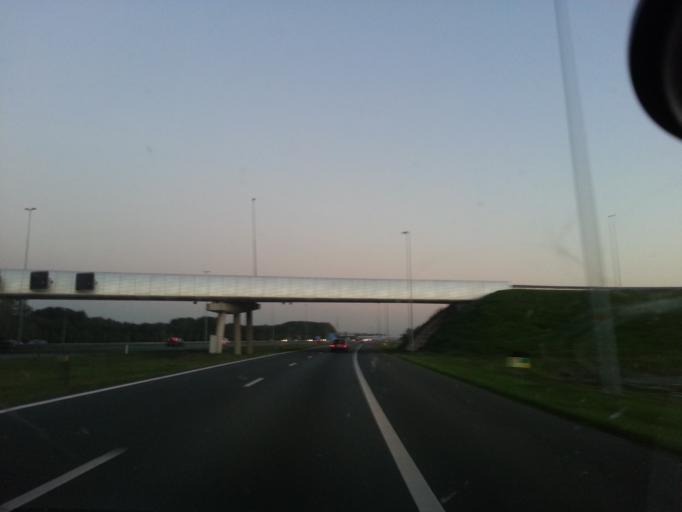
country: NL
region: Utrecht
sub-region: Gemeente Vianen
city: Vianen
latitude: 51.9740
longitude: 5.1046
